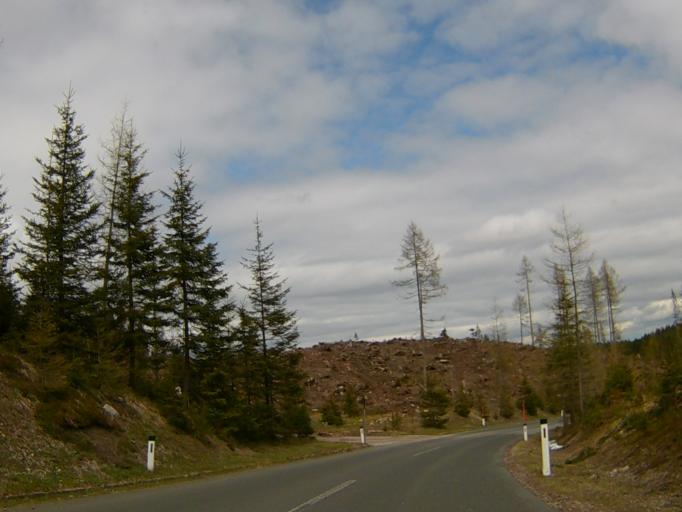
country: AT
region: Carinthia
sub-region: Politischer Bezirk Villach Land
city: Arnoldstein
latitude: 46.5924
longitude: 13.7287
